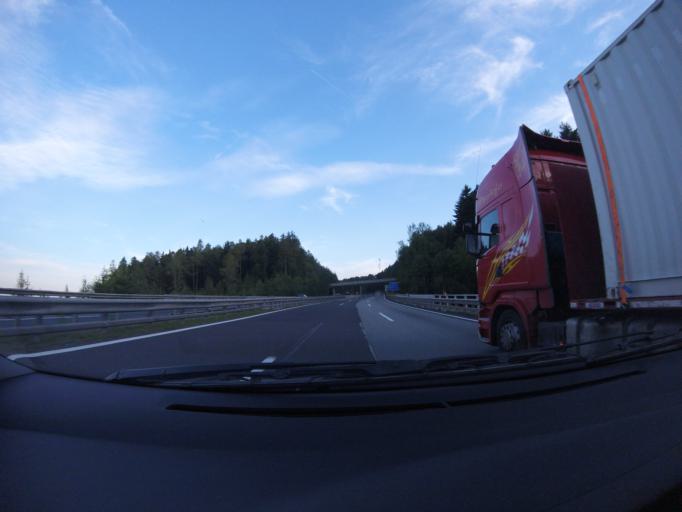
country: AT
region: Lower Austria
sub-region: Politischer Bezirk Neunkirchen
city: Thomasberg
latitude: 47.5544
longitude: 16.1301
